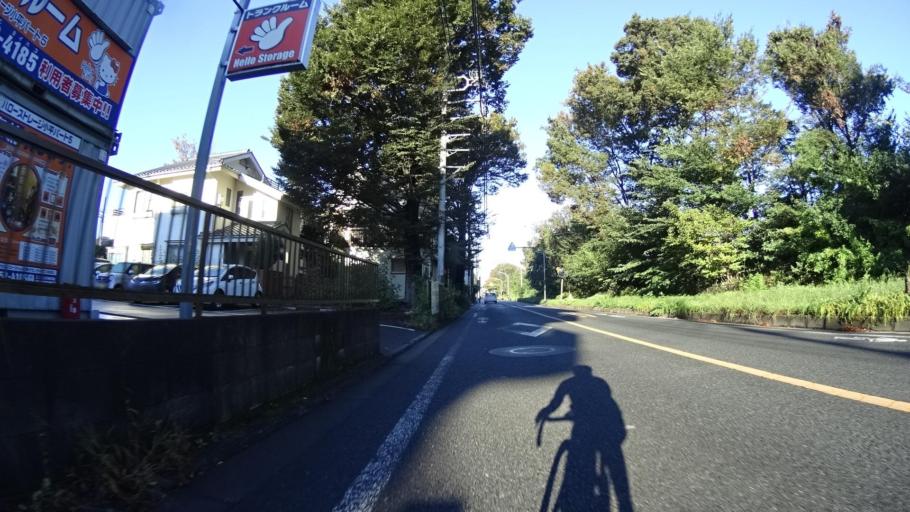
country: JP
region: Tokyo
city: Kokubunji
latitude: 35.7154
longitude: 139.4858
